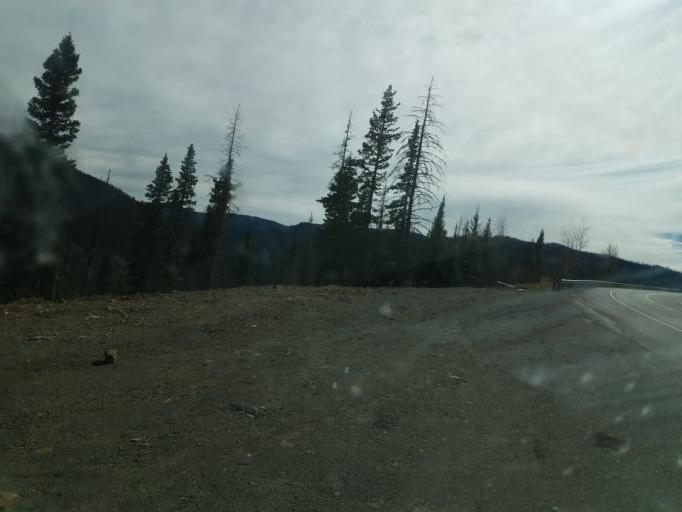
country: US
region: Colorado
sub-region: Archuleta County
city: Pagosa Springs
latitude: 37.4930
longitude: -106.7659
